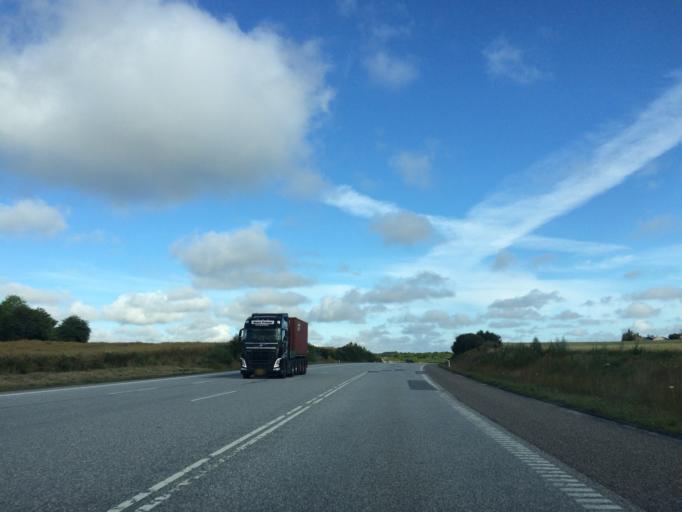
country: DK
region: Central Jutland
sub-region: Silkeborg Kommune
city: Kjellerup
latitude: 56.3361
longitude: 9.5400
